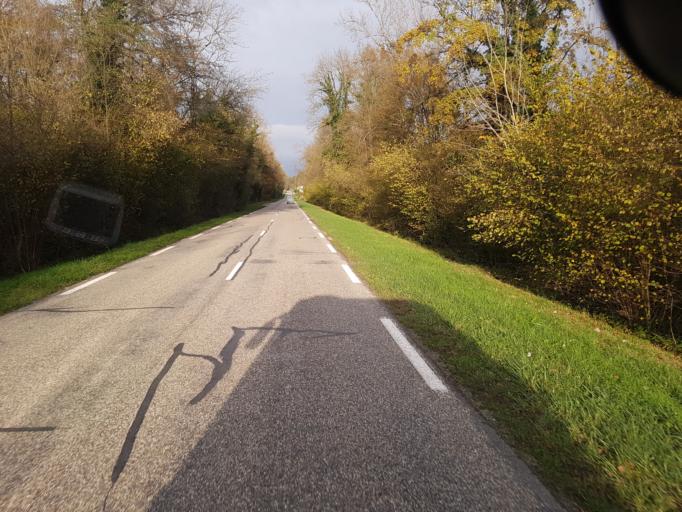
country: FR
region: Rhone-Alpes
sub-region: Departement de la Haute-Savoie
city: Frangy
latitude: 45.9977
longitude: 5.8544
